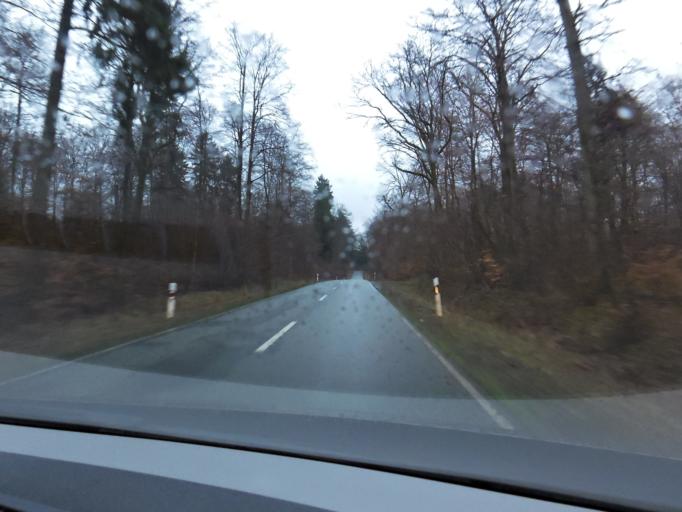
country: DE
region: Schleswig-Holstein
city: Schmilau
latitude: 53.6605
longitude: 10.7933
